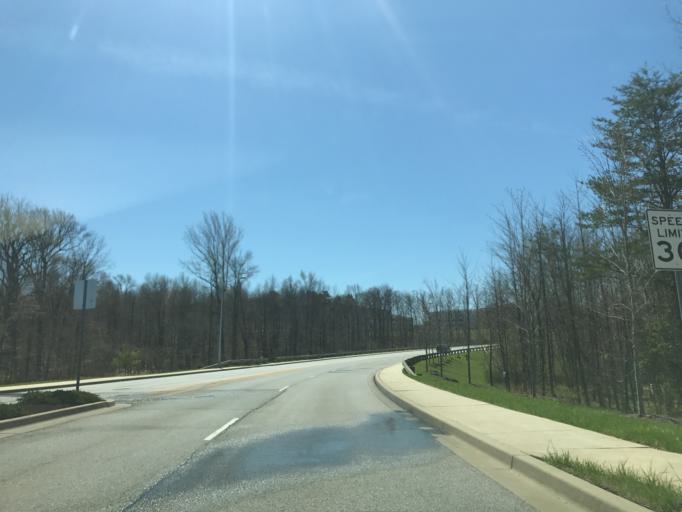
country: US
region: Maryland
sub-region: Anne Arundel County
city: Jessup
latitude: 39.1309
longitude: -76.7695
